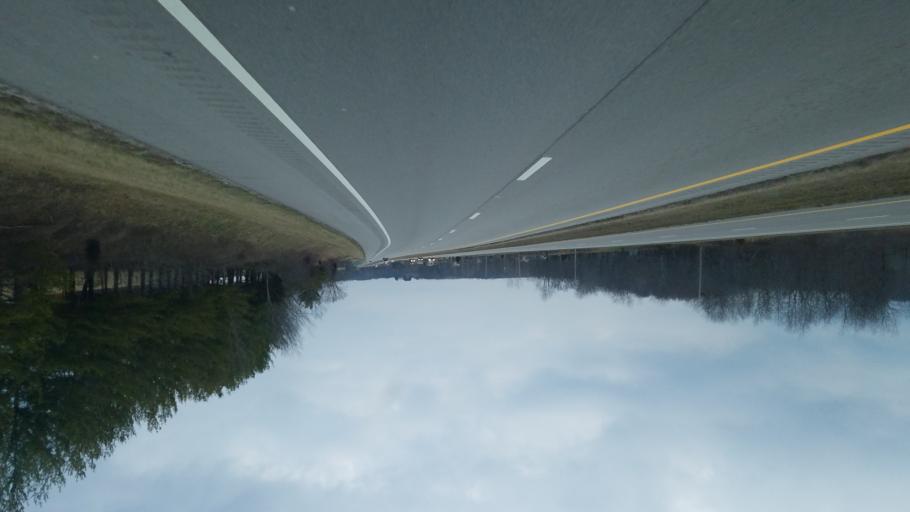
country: US
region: Ohio
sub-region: Jackson County
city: Oak Hill
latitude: 38.8870
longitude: -82.4276
